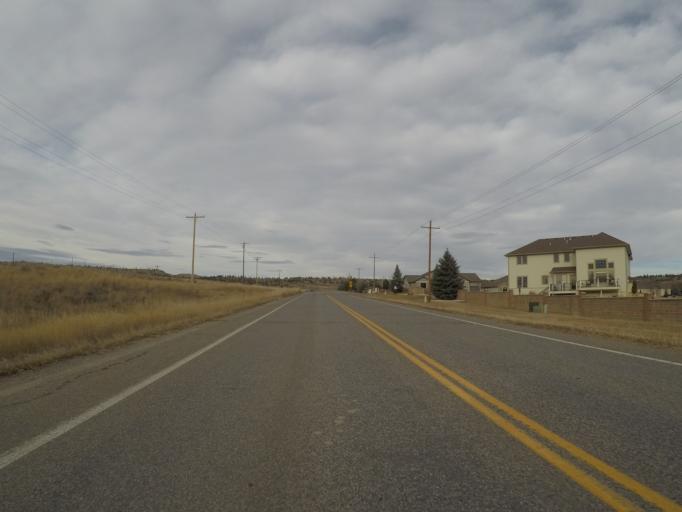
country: US
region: Montana
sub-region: Yellowstone County
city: Laurel
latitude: 45.8070
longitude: -108.6737
